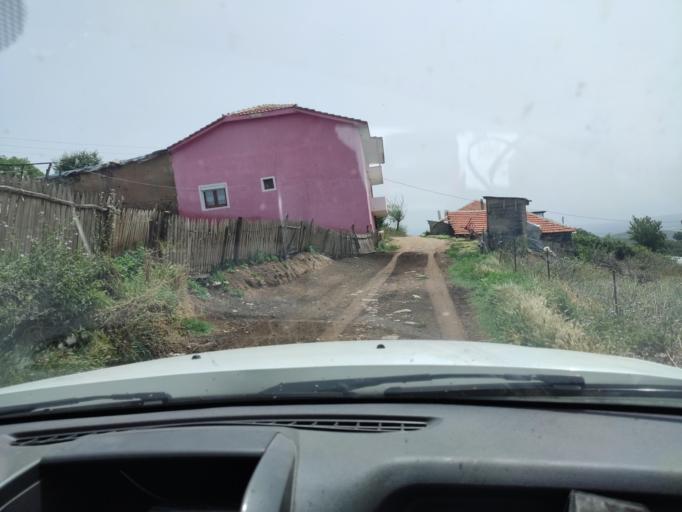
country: MK
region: Radovis
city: Radovish
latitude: 41.6795
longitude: 22.4027
